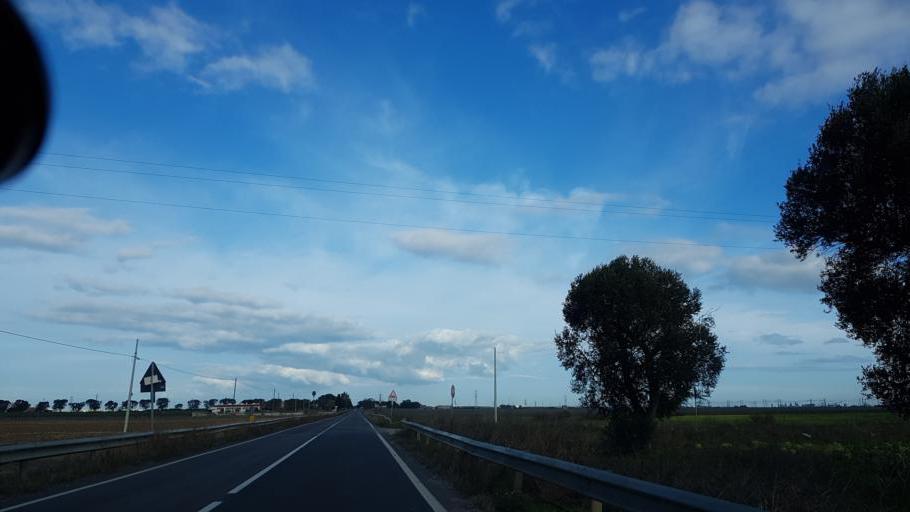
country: IT
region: Apulia
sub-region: Provincia di Brindisi
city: Tuturano
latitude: 40.5736
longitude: 17.9673
